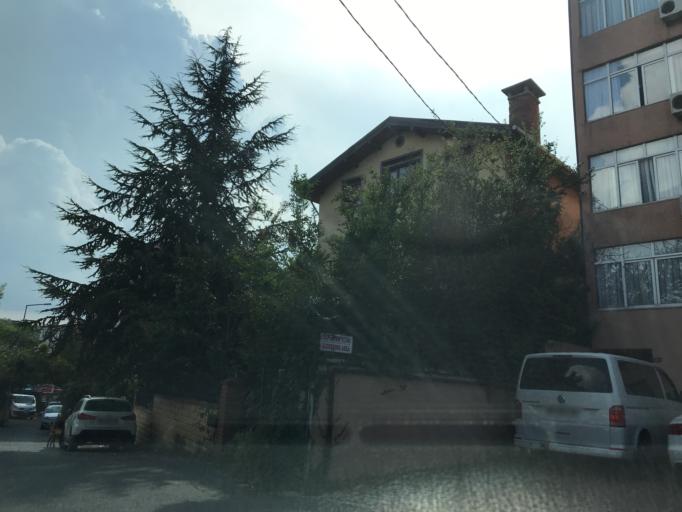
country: TR
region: Istanbul
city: Arikoey
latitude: 41.2470
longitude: 29.0361
